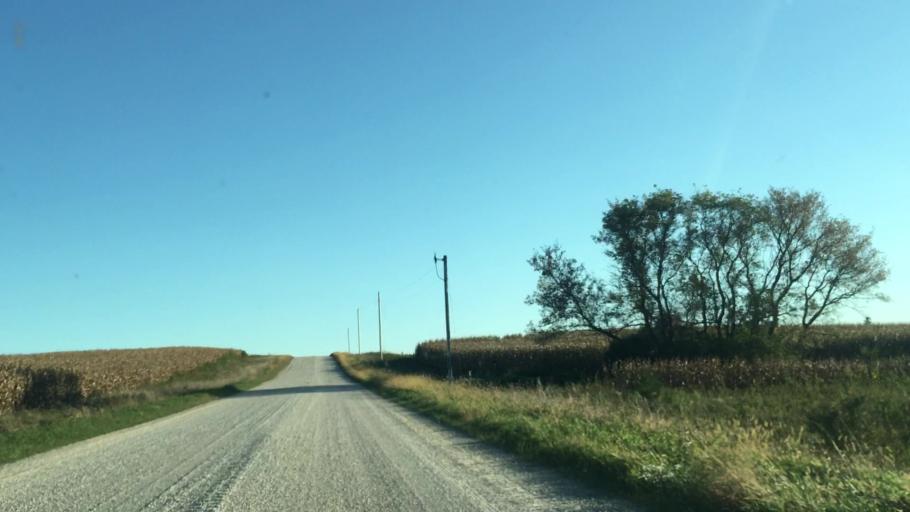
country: US
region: Minnesota
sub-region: Fillmore County
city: Preston
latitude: 43.7969
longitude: -92.0394
